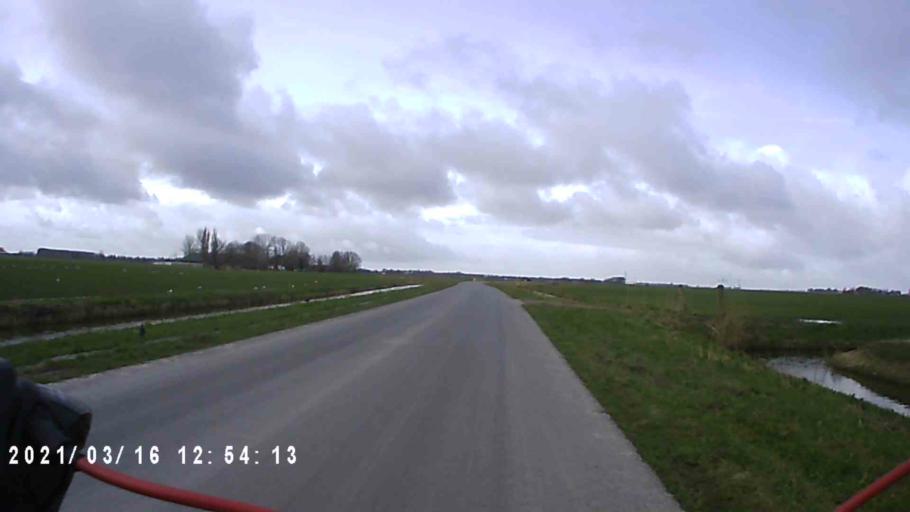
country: NL
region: Friesland
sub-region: Menameradiel
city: Berltsum
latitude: 53.2551
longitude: 5.6726
